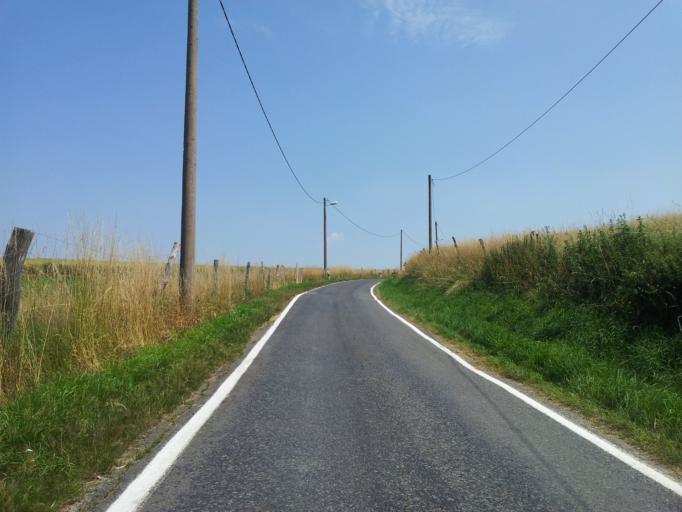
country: DE
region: Saxony
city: Panschwitz-Kuckau
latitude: 51.2065
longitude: 14.2013
